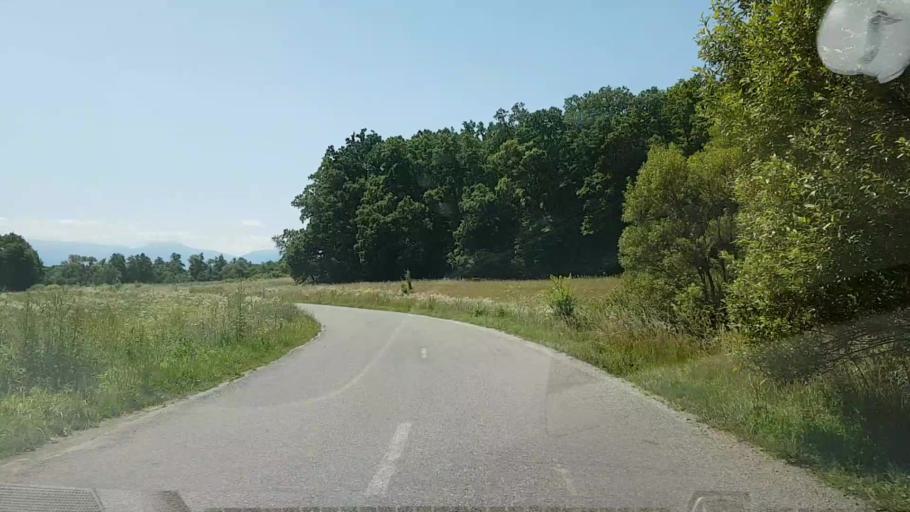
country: RO
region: Brasov
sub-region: Comuna Cincu
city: Cincu
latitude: 45.8821
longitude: 24.8135
